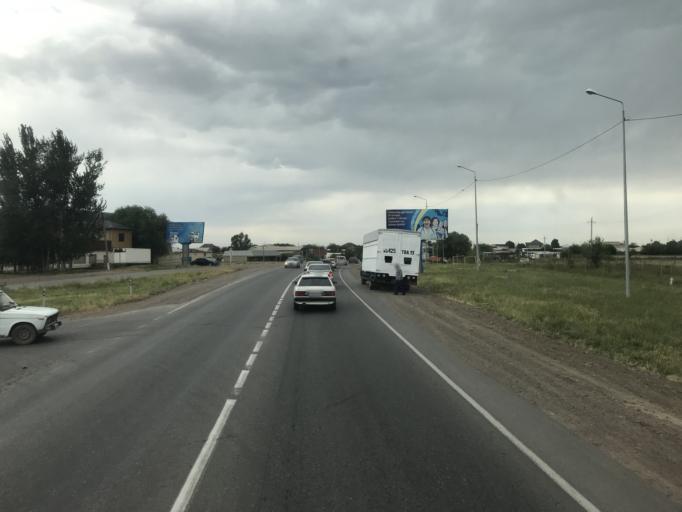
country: KZ
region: Ongtustik Qazaqstan
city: Saryaghash
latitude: 41.4334
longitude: 69.1134
